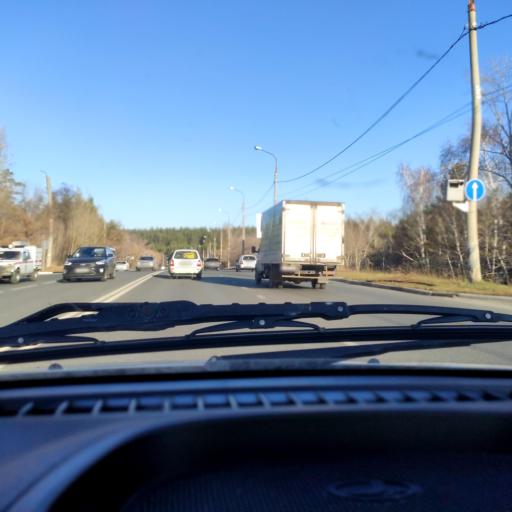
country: RU
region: Samara
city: Zhigulevsk
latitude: 53.4988
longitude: 49.4728
